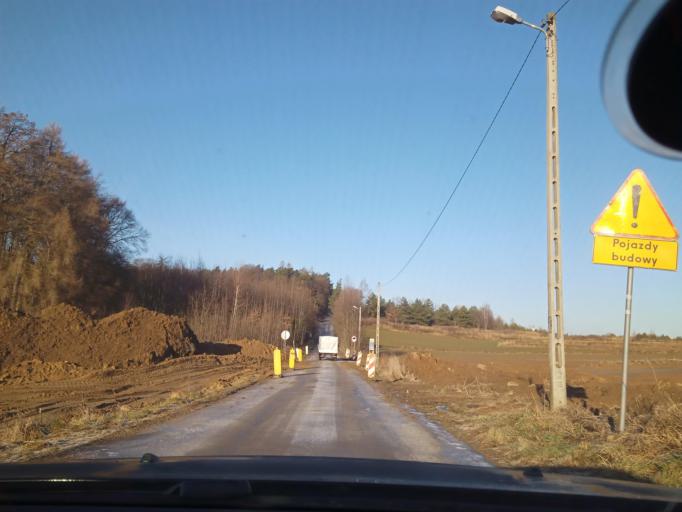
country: PL
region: Lesser Poland Voivodeship
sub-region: Powiat krakowski
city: Michalowice
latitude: 50.1946
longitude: 20.0207
